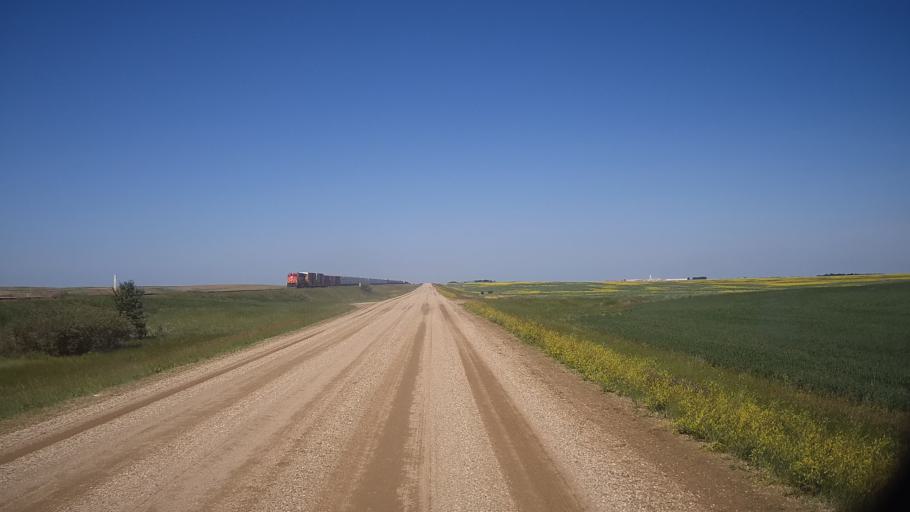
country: CA
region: Saskatchewan
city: Watrous
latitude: 51.8548
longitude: -105.9468
